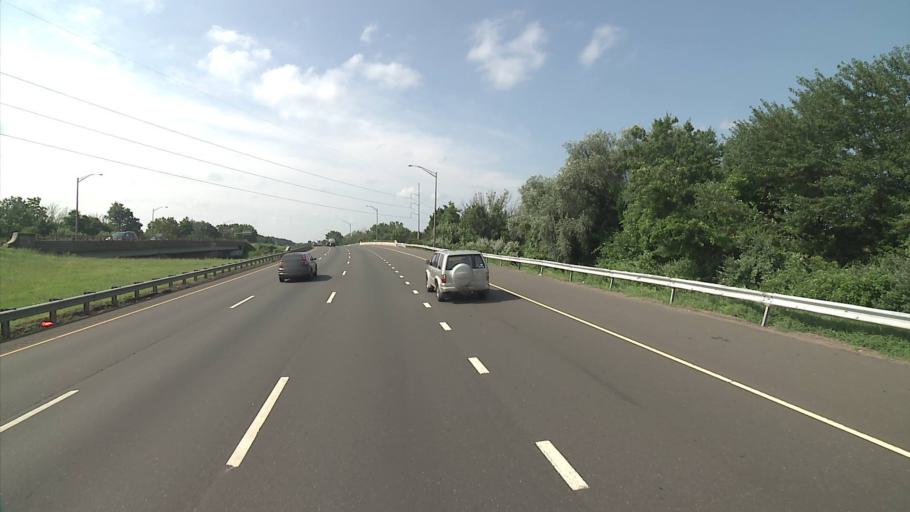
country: US
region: Connecticut
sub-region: New Haven County
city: North Haven
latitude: 41.3918
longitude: -72.8649
